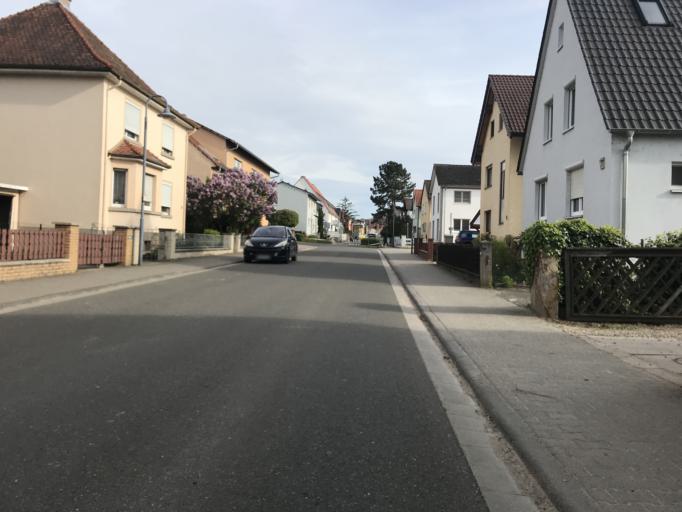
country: DE
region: Rheinland-Pfalz
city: Gau-Algesheim
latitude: 49.9622
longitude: 8.0113
